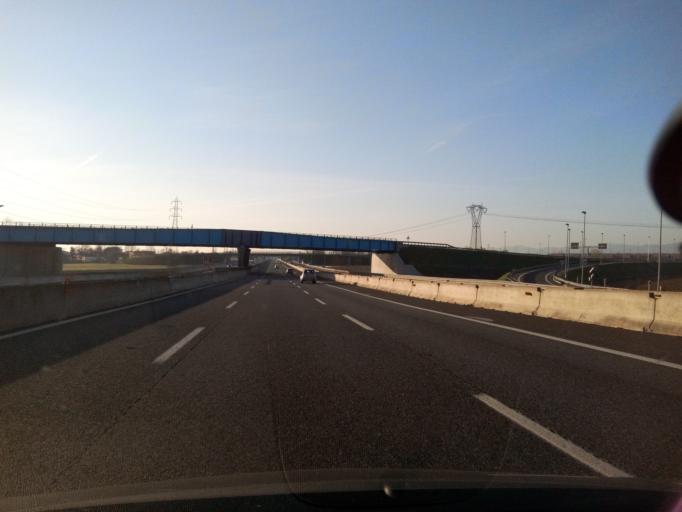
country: IT
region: Emilia-Romagna
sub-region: Provincia di Piacenza
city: Piacenza
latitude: 45.0583
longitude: 9.7414
